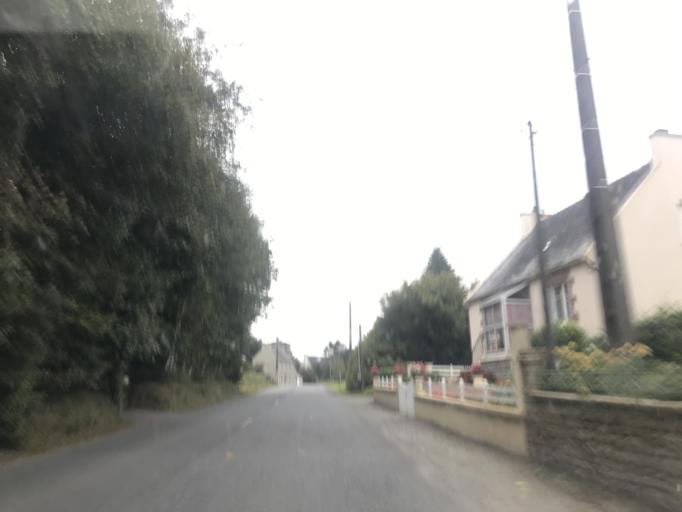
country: FR
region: Brittany
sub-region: Departement du Finistere
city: Plouneour-Menez
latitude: 48.4094
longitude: -3.9569
